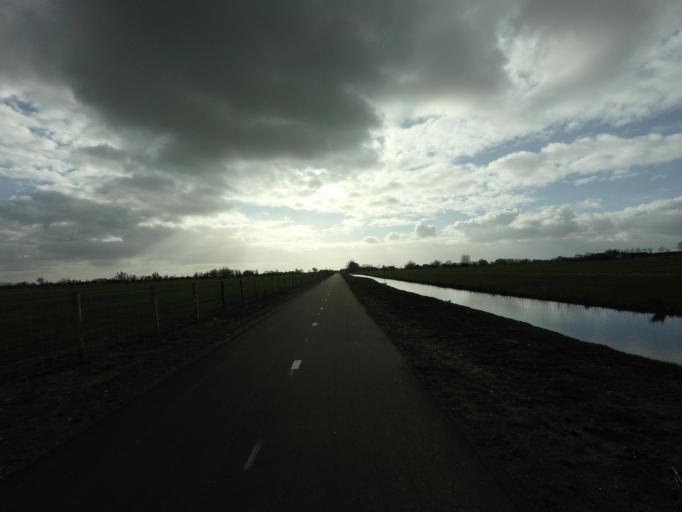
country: NL
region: Utrecht
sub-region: Gemeente IJsselstein
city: IJsselstein
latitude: 52.0525
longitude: 5.0252
